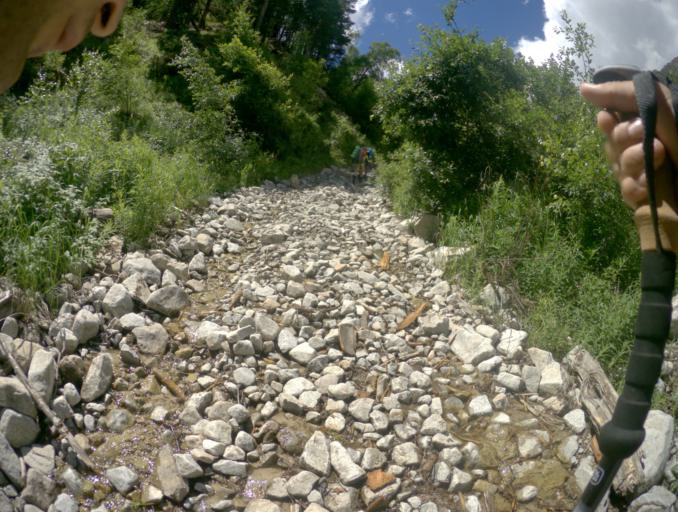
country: RU
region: Karachayevo-Cherkesiya
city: Uchkulan
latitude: 43.3545
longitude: 42.1755
